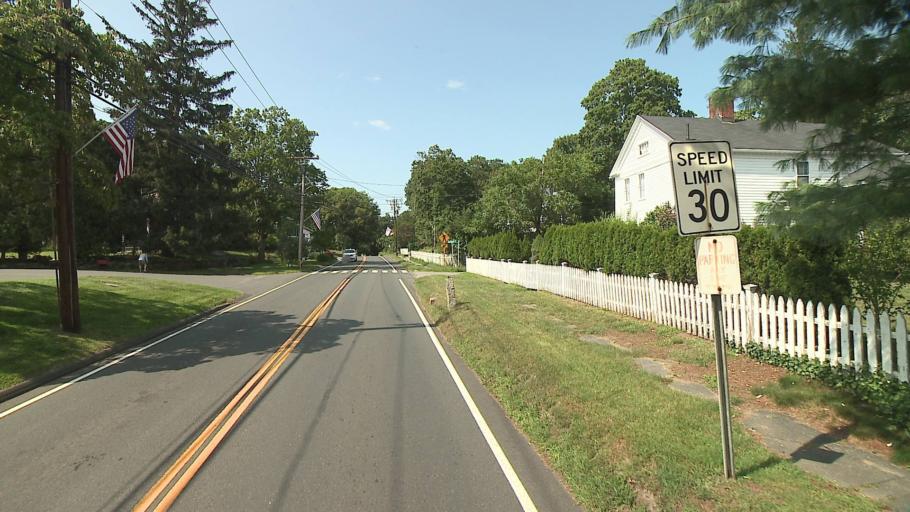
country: US
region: Connecticut
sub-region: Fairfield County
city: Danbury
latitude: 41.4663
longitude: -73.3880
